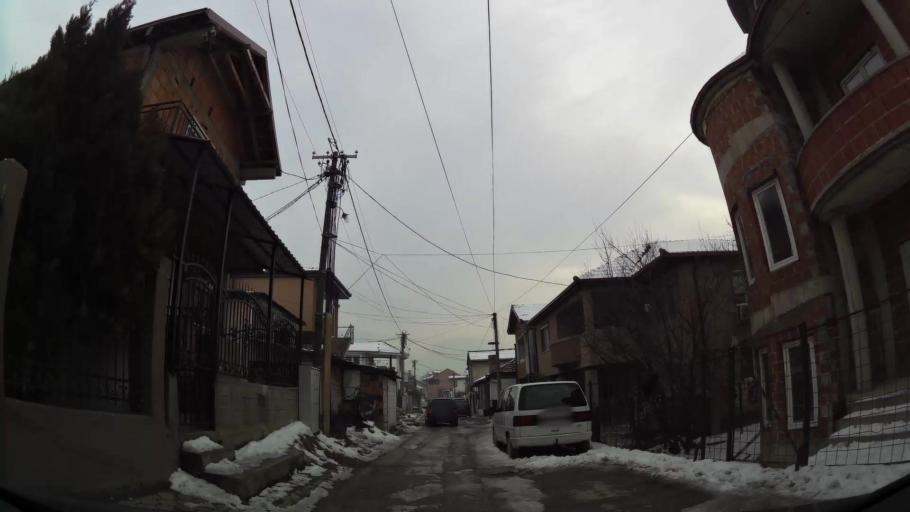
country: MK
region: Suto Orizari
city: Suto Orizare
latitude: 42.0378
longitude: 21.4273
